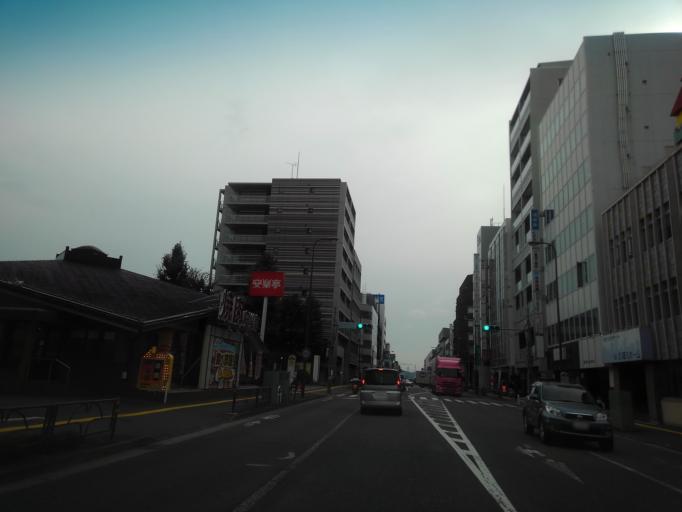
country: JP
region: Tokyo
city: Hino
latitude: 35.6944
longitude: 139.4190
